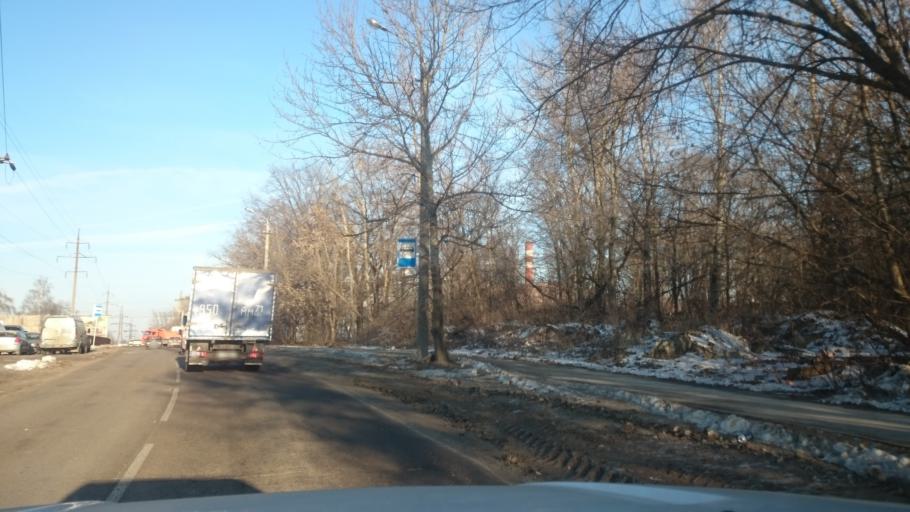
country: RU
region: Tula
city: Tula
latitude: 54.2193
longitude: 37.6852
